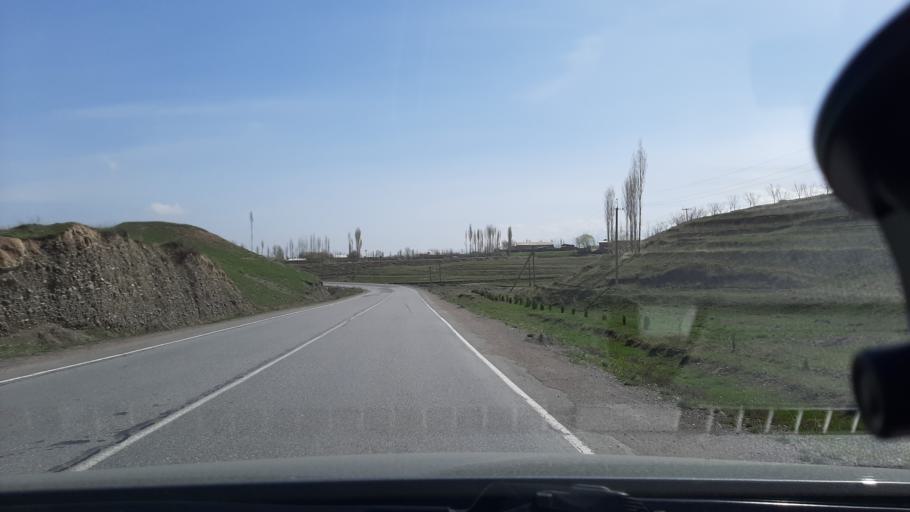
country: TJ
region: Viloyati Sughd
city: Shahriston
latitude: 39.7802
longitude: 68.8414
